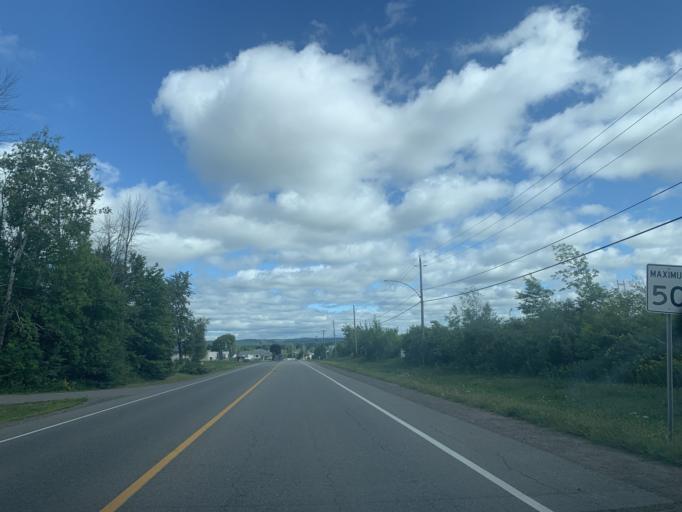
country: CA
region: Ontario
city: Hawkesbury
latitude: 45.6000
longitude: -74.5865
